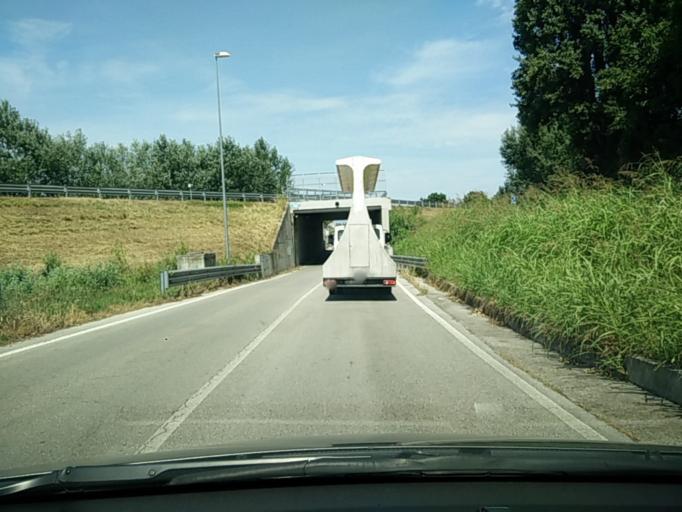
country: IT
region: Veneto
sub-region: Provincia di Venezia
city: Passarella
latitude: 45.5987
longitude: 12.5942
